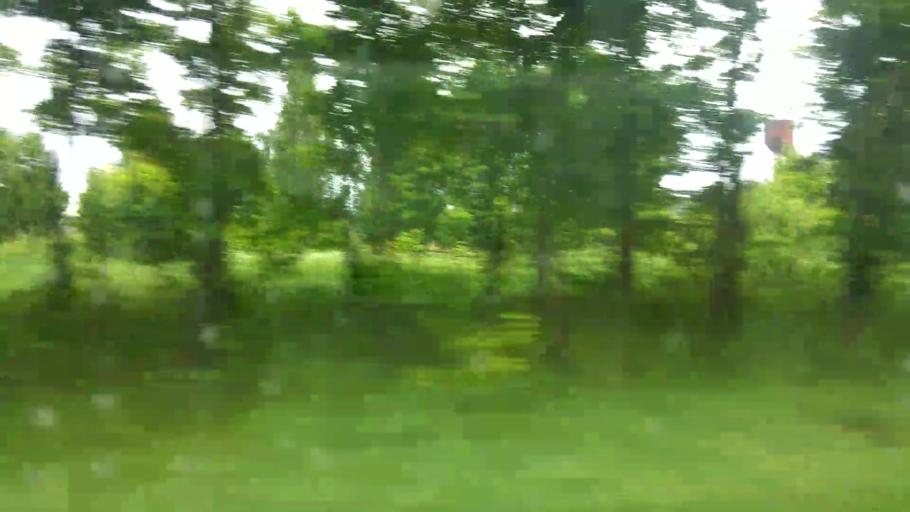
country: RU
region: Moskovskaya
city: Ozherel'ye
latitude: 54.8407
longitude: 38.2722
